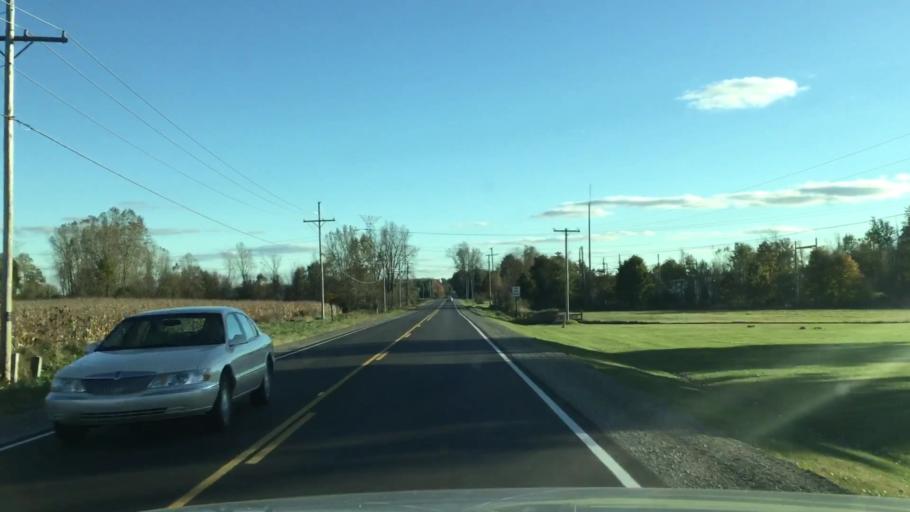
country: US
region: Michigan
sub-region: Lapeer County
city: Almont
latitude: 42.9416
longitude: -83.1447
